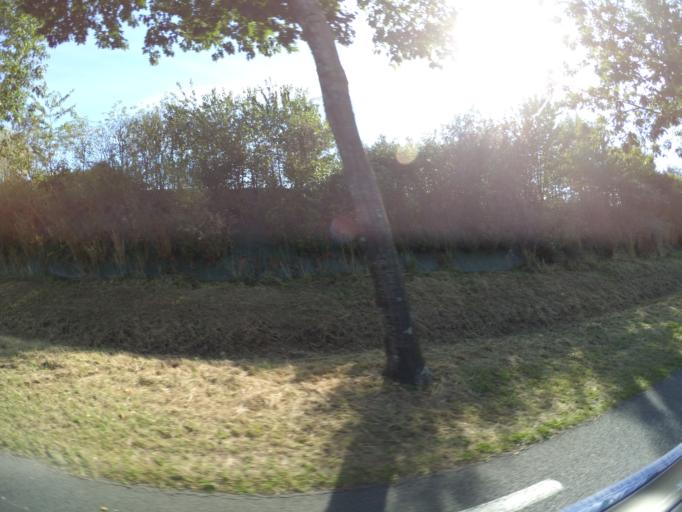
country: FR
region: Pays de la Loire
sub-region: Departement de Maine-et-Loire
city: Cholet
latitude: 47.0655
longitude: -0.9058
